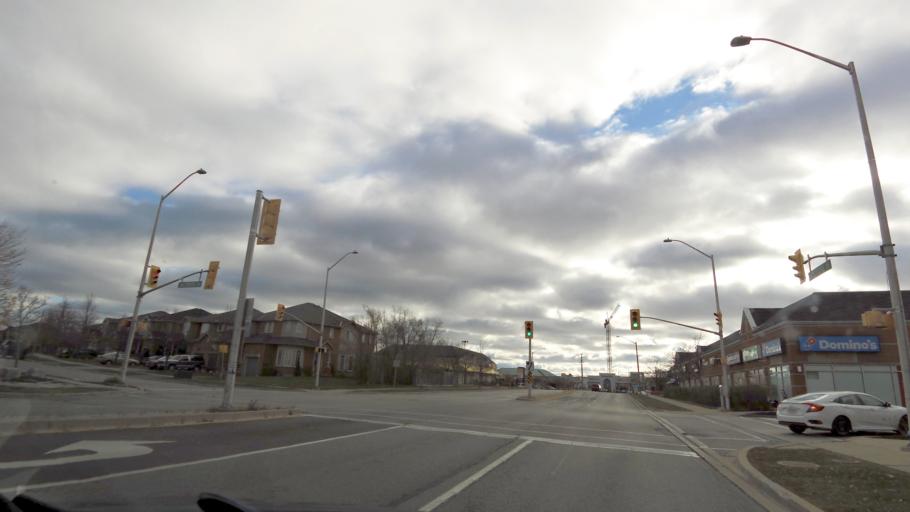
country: CA
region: Ontario
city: Oakville
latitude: 43.4857
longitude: -79.7135
